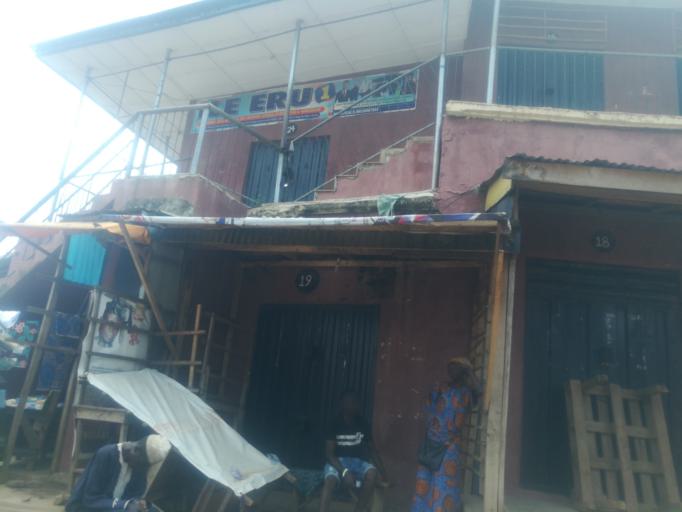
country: NG
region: Oyo
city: Ibadan
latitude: 7.3874
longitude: 3.8844
